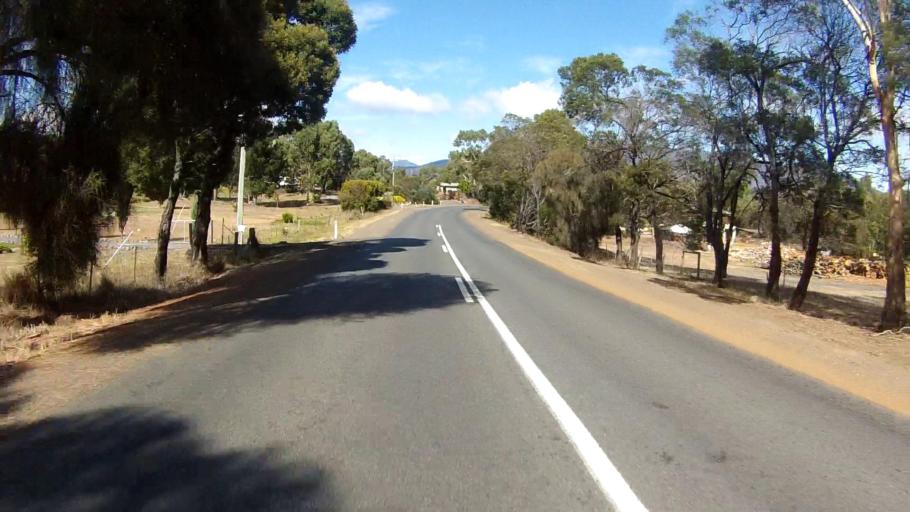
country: AU
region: Tasmania
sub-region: Brighton
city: Old Beach
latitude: -42.7691
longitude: 147.2720
